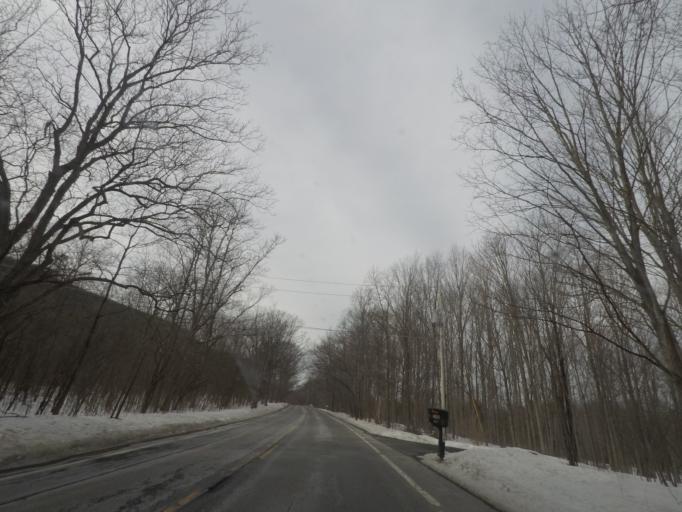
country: US
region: New York
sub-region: Albany County
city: Altamont
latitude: 42.6701
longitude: -74.0072
